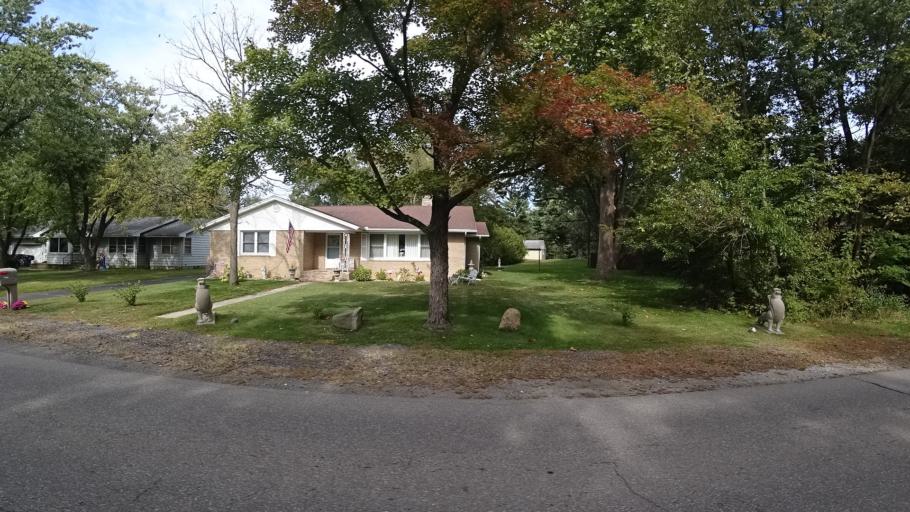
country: US
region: Indiana
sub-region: LaPorte County
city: Trail Creek
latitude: 41.7168
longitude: -86.8670
